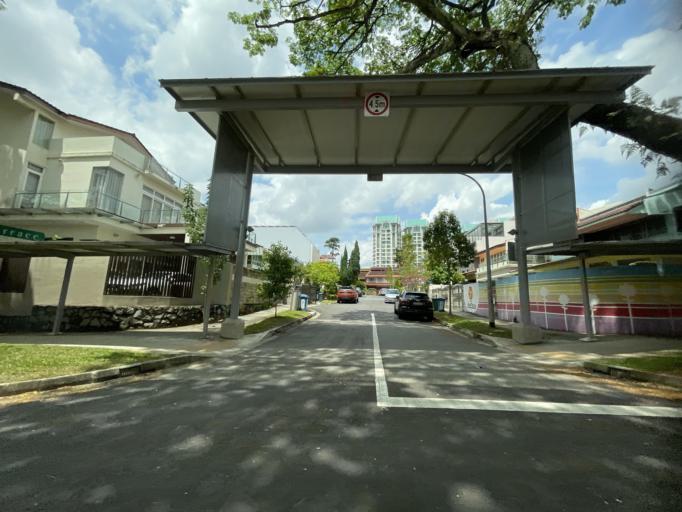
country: MY
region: Johor
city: Johor Bahru
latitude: 1.3707
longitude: 103.7660
